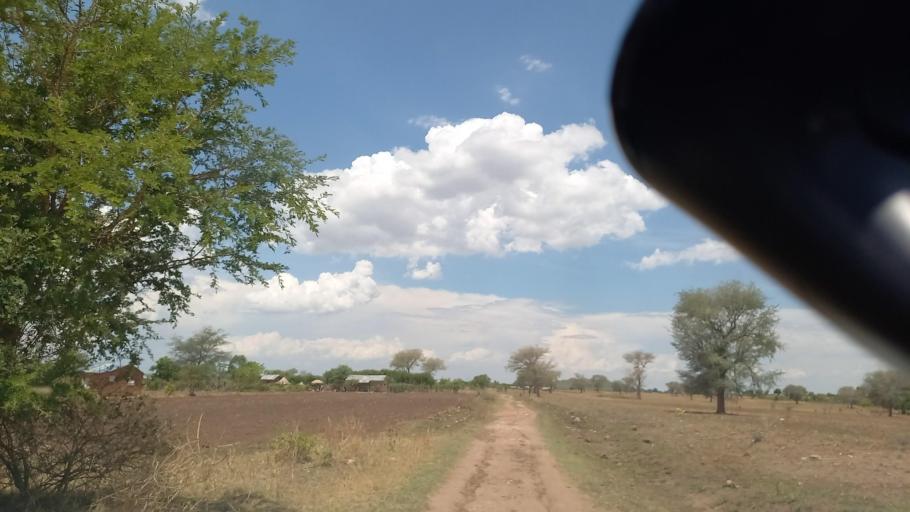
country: ZM
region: Southern
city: Mazabuka
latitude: -16.1097
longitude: 27.8191
